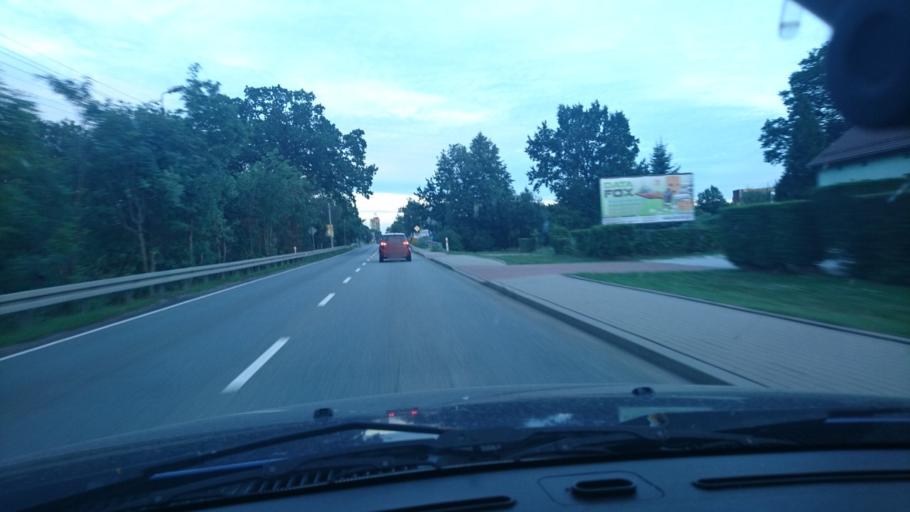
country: PL
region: Silesian Voivodeship
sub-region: Powiat tarnogorski
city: Zbroslawice
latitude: 50.4821
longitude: 18.7892
